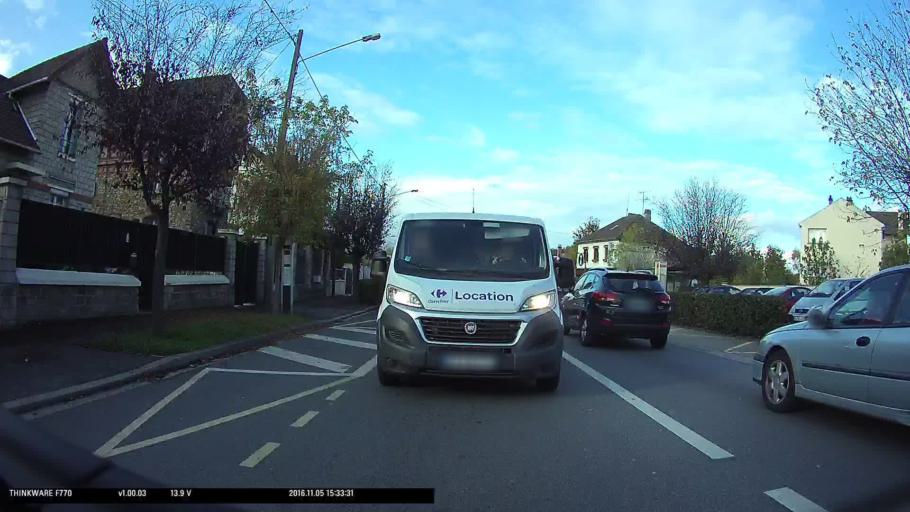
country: FR
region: Ile-de-France
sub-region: Departement des Yvelines
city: Meulan-en-Yvelines
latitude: 49.0087
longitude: 1.9050
